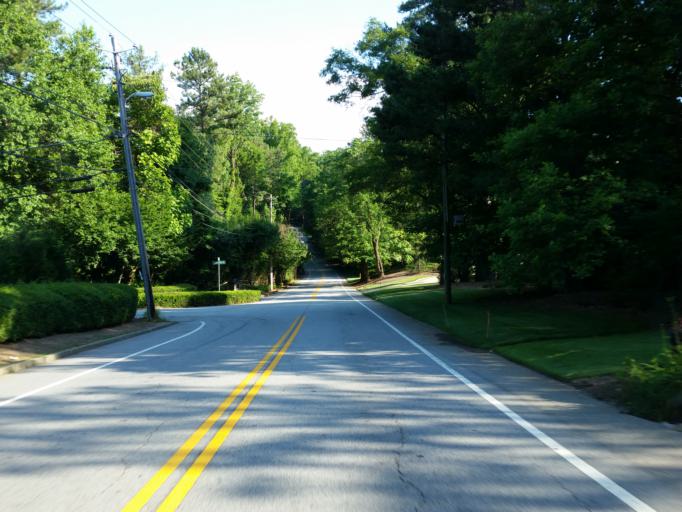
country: US
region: Georgia
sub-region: Cobb County
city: Vinings
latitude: 33.8879
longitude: -84.4265
